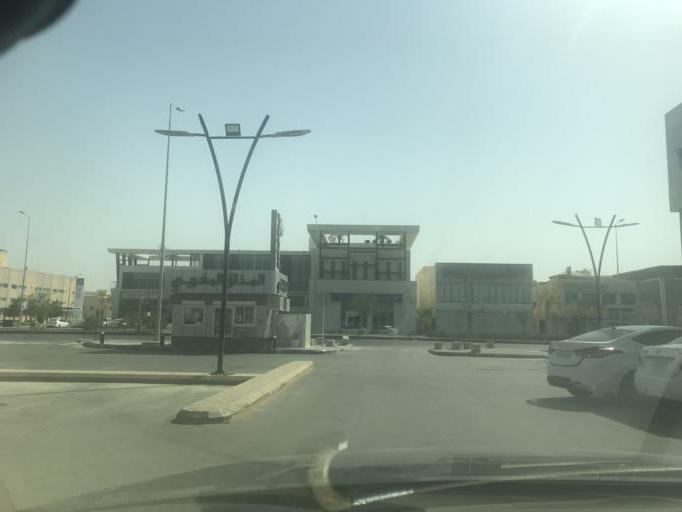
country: SA
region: Ar Riyad
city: Riyadh
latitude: 24.7356
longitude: 46.7838
